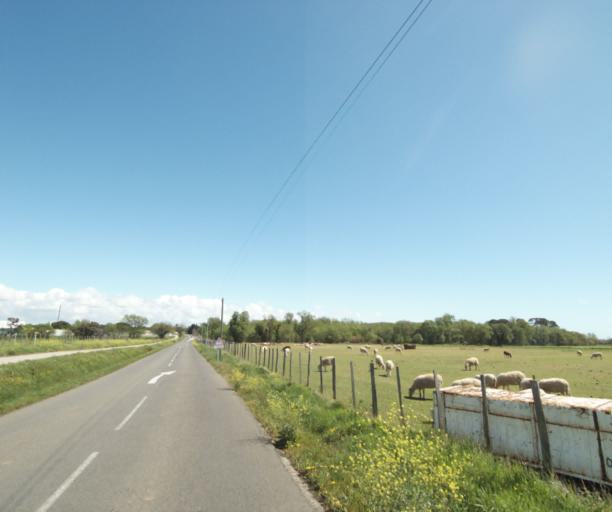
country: FR
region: Languedoc-Roussillon
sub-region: Departement de l'Herault
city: Perols
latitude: 43.5581
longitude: 3.9317
